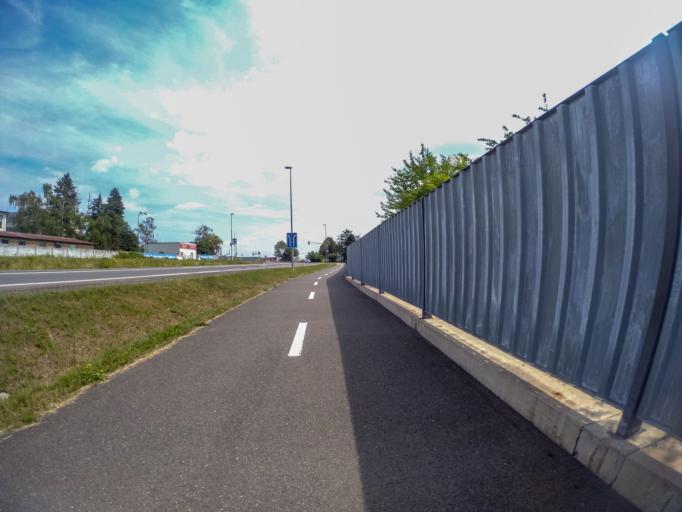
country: CZ
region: Praha
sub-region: Praha 19
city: Kbely
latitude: 50.1291
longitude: 14.5408
